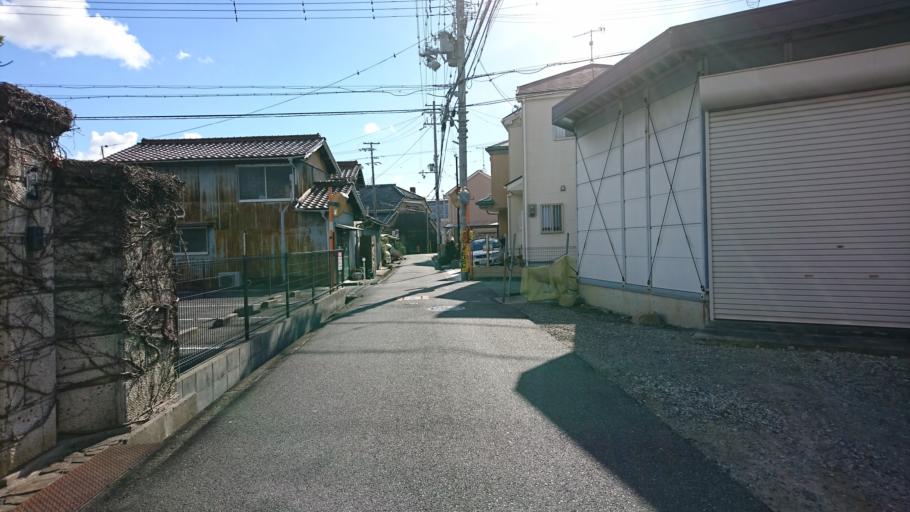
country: JP
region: Hyogo
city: Kakogawacho-honmachi
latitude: 34.7544
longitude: 134.8432
